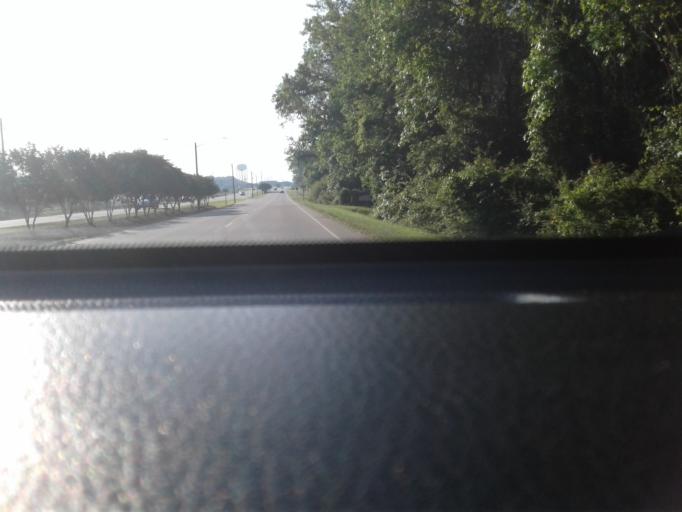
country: US
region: North Carolina
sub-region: Harnett County
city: Erwin
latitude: 35.3223
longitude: -78.6413
